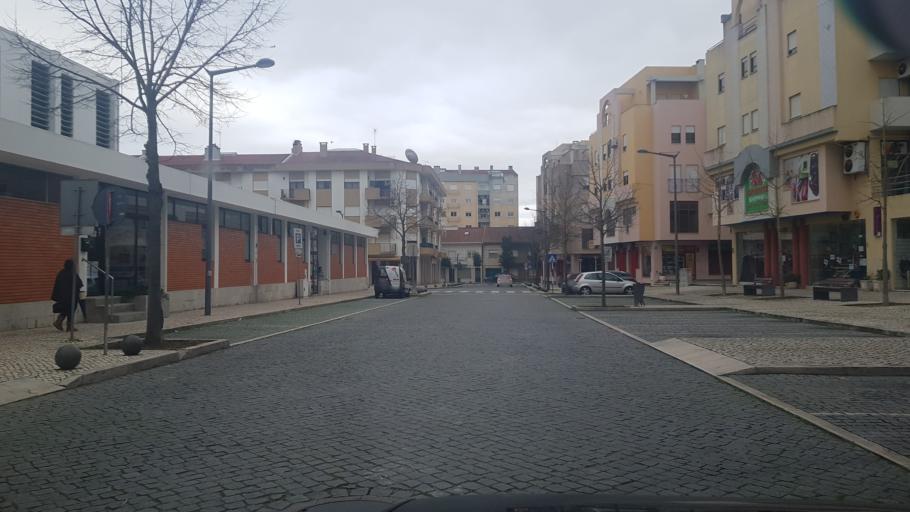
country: PT
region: Santarem
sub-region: Entroncamento
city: Entroncamento
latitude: 39.4616
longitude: -8.4708
